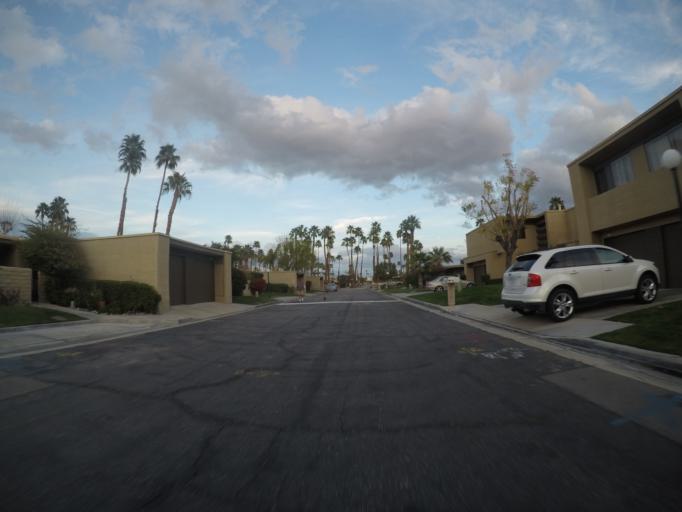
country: US
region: California
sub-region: Riverside County
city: Palm Springs
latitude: 33.8182
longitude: -116.5336
